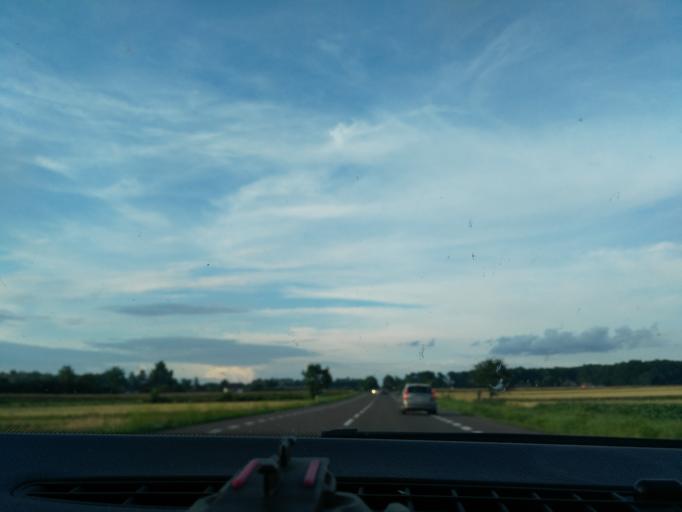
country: PL
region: Lublin Voivodeship
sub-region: Powiat krasnicki
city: Wilkolaz
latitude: 51.0218
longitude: 22.3588
